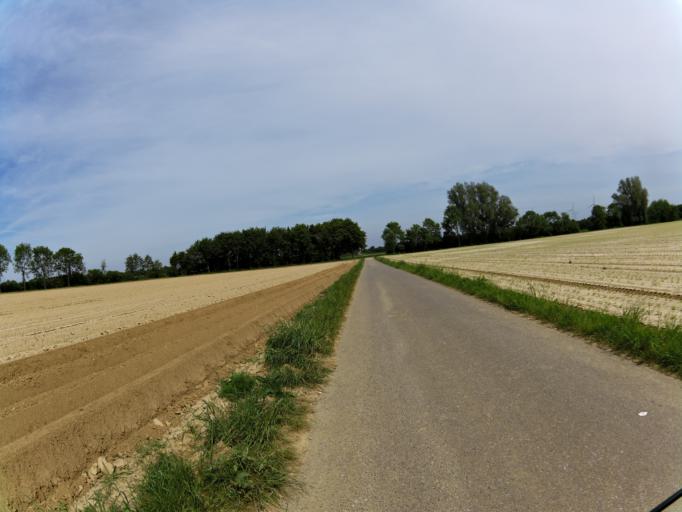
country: DE
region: North Rhine-Westphalia
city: Niedermerz
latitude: 50.8769
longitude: 6.2503
